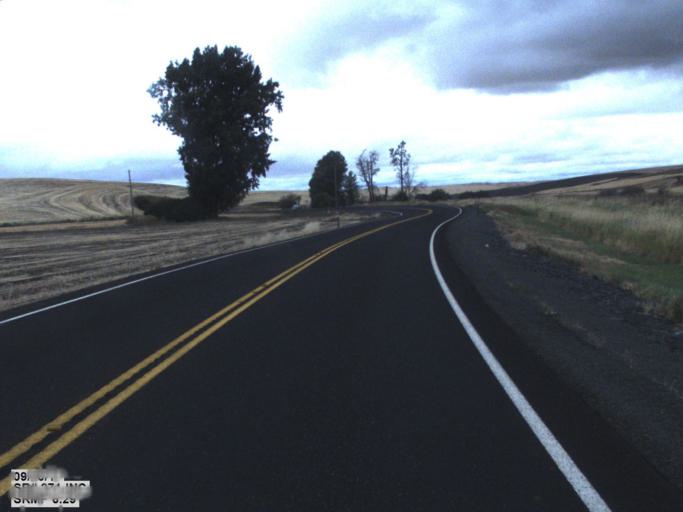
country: US
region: Washington
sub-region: Whitman County
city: Colfax
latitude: 47.1880
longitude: -117.3317
